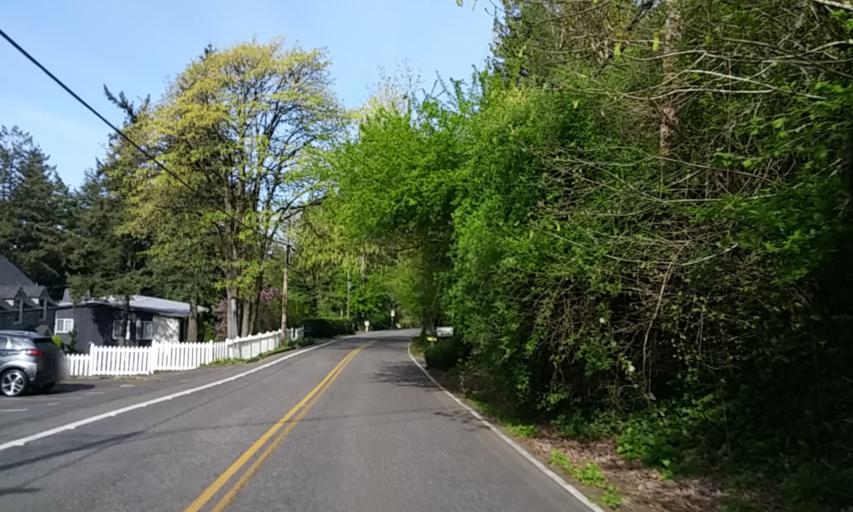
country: US
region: Oregon
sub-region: Washington County
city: West Slope
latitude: 45.4990
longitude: -122.7635
